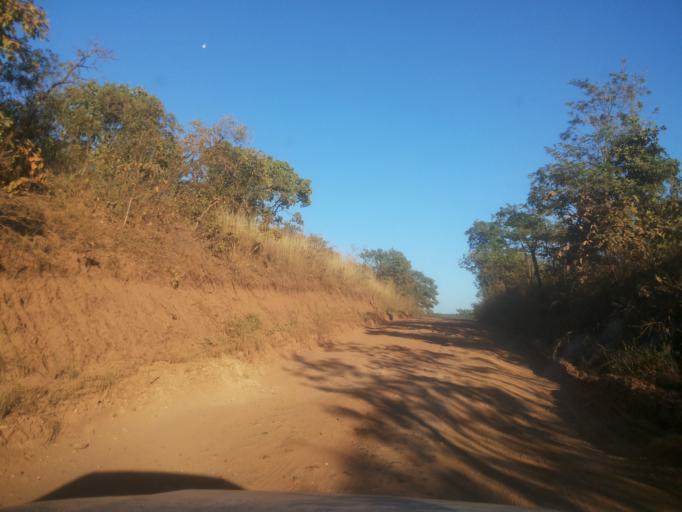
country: BR
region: Minas Gerais
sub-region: Campina Verde
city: Campina Verde
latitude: -19.3271
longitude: -49.7883
